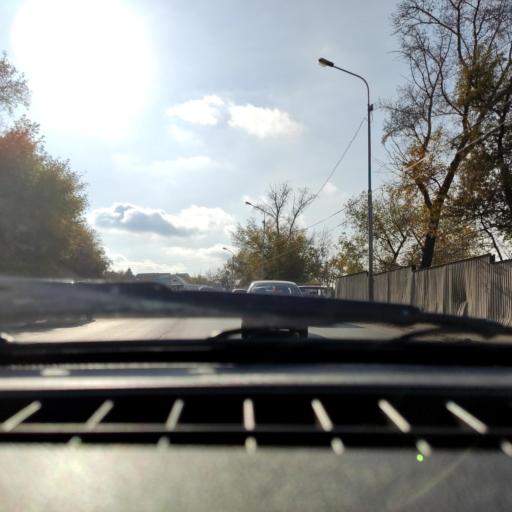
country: RU
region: Bashkortostan
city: Ufa
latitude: 54.7422
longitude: 55.9321
